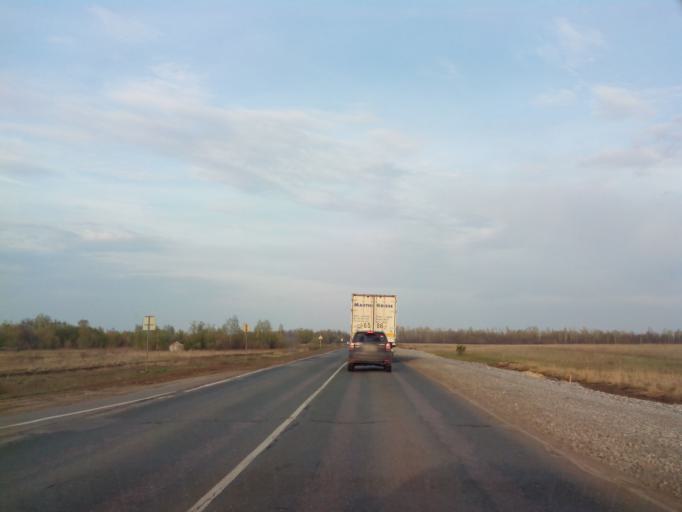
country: RU
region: Rjazan
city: Zarechnyy
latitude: 53.7522
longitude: 39.8205
